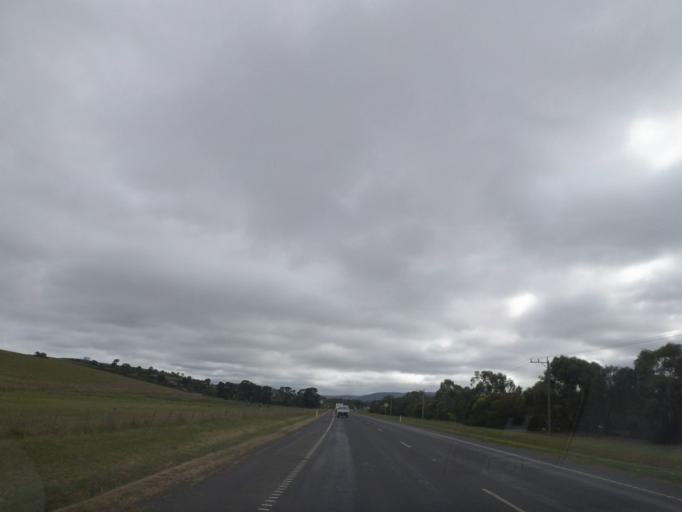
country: AU
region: Victoria
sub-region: Whittlesea
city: Whittlesea
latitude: -37.5286
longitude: 145.1125
